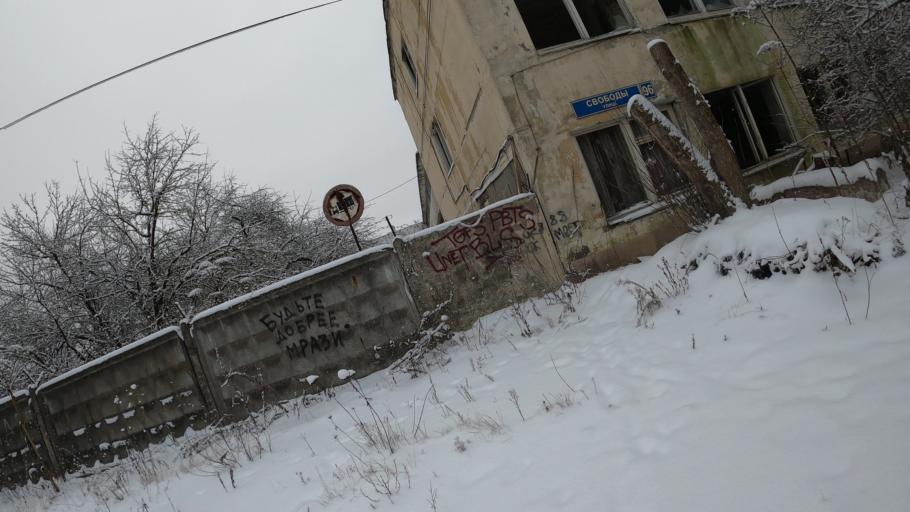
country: RU
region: Jaroslavl
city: Pereslavl'-Zalesskiy
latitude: 56.7397
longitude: 38.8936
